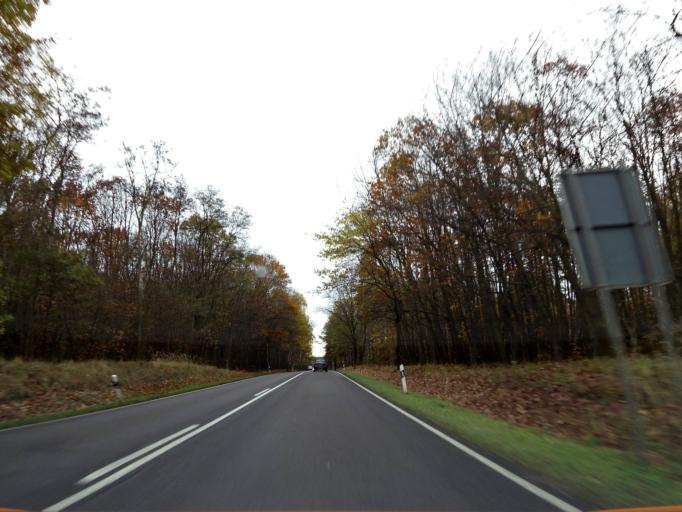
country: DE
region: Saxony-Anhalt
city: Letzlingen
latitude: 52.4062
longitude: 11.4760
